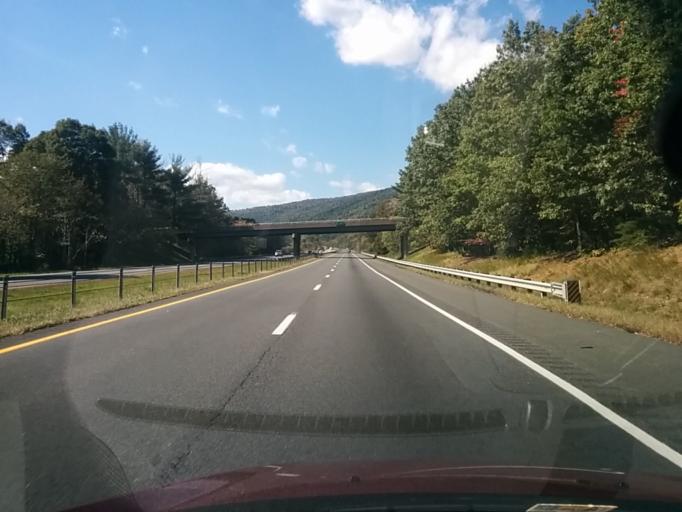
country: US
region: Virginia
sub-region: Albemarle County
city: Crozet
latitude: 38.0445
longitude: -78.7583
